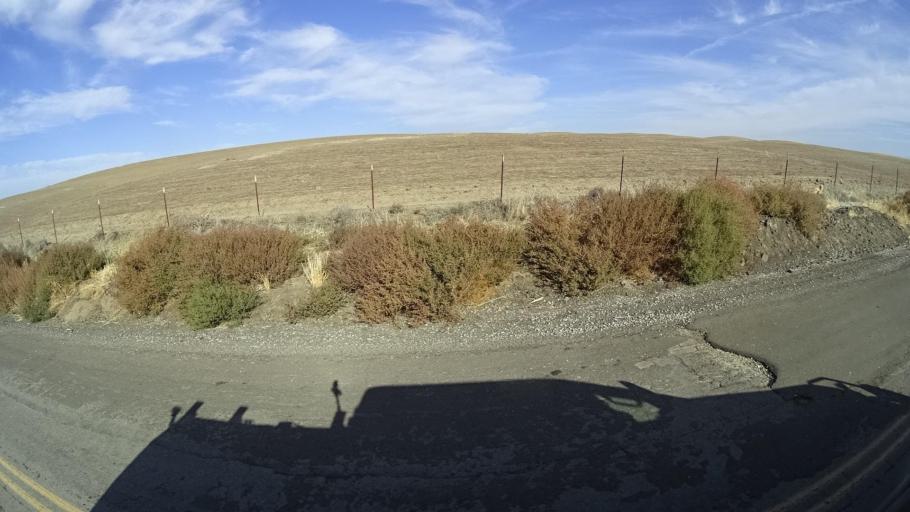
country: US
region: California
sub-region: Tulare County
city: Richgrove
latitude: 35.6219
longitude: -119.0133
